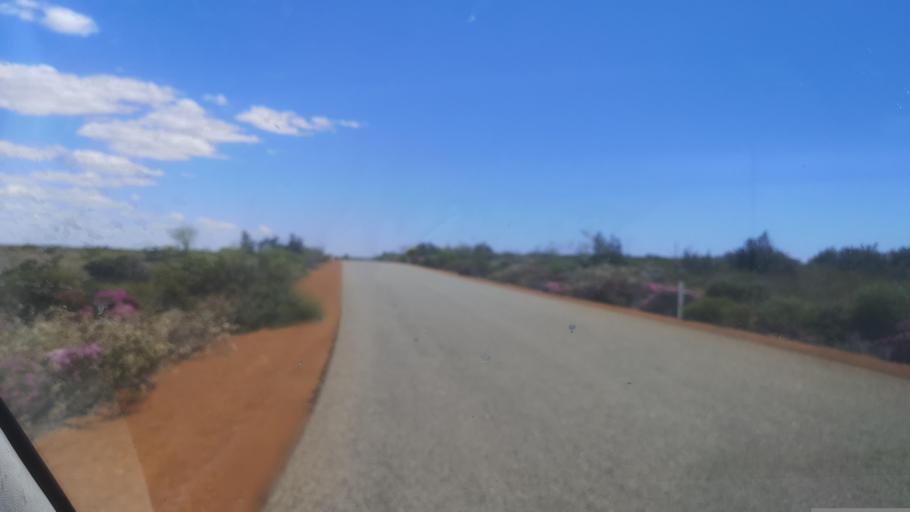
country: AU
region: Western Australia
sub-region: Northampton Shire
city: Kalbarri
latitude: -27.8121
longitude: 114.4653
